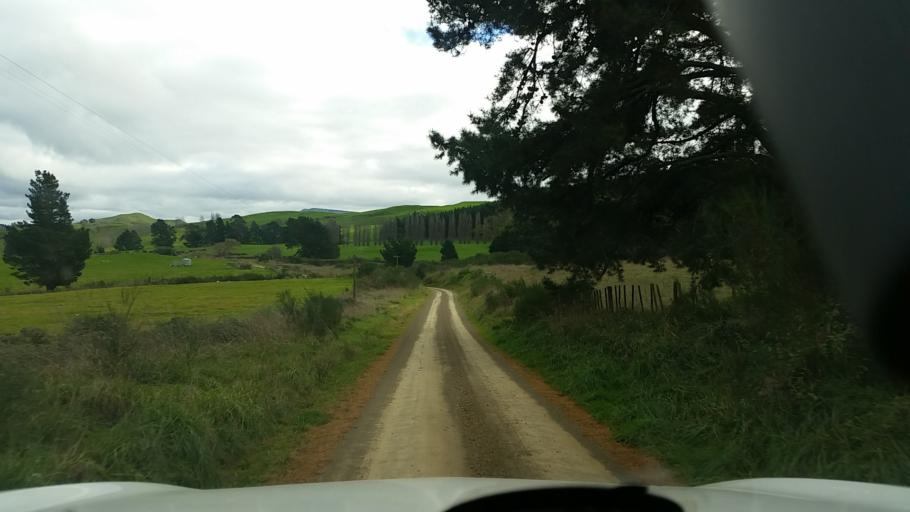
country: NZ
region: Hawke's Bay
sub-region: Napier City
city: Napier
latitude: -39.1988
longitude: 176.8786
